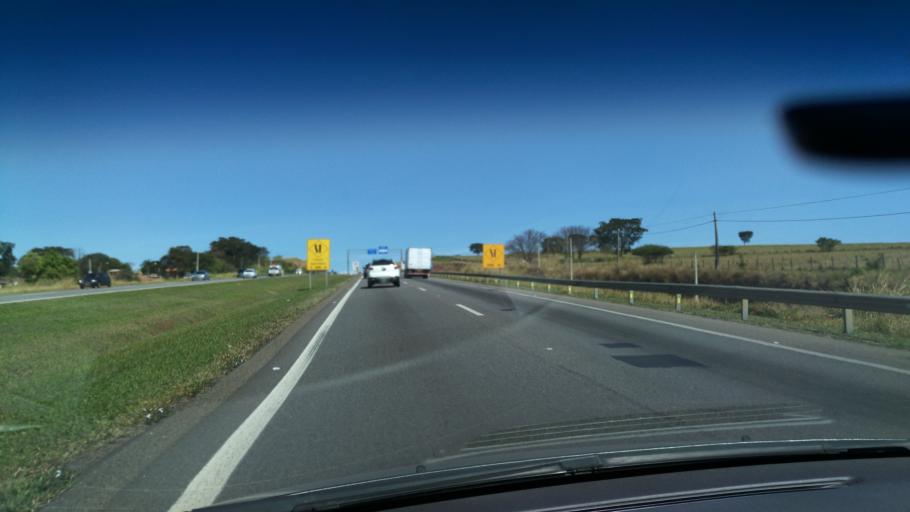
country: BR
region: Sao Paulo
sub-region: Jaguariuna
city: Jaguariuna
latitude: -22.7550
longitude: -47.0209
